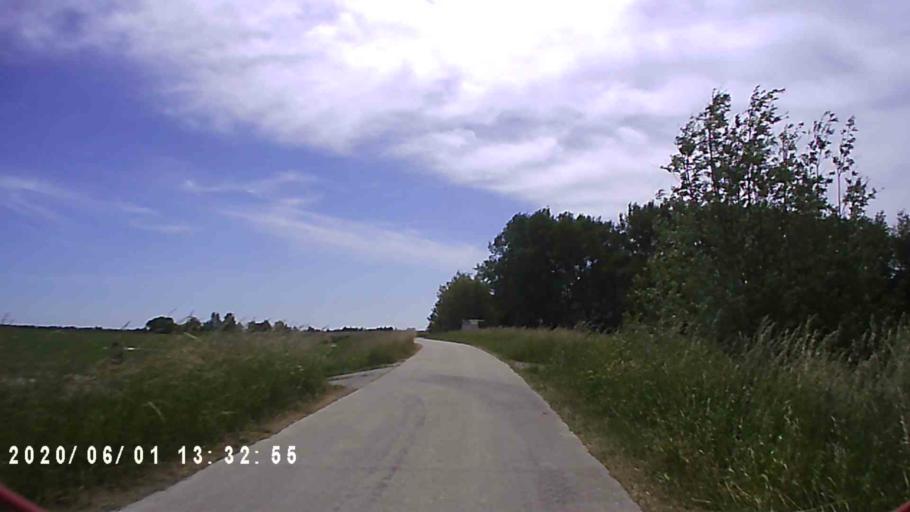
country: NL
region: Friesland
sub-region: Gemeente Littenseradiel
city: Wommels
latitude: 53.0923
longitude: 5.5689
